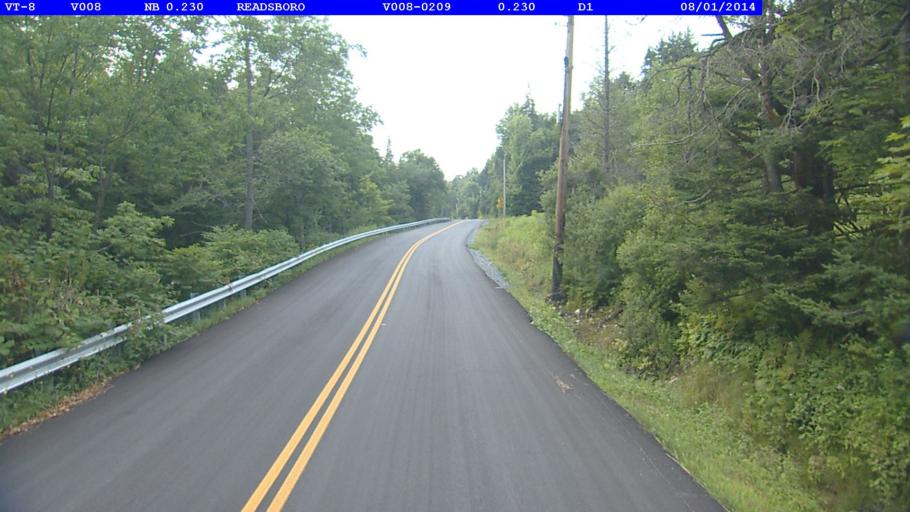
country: US
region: Massachusetts
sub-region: Berkshire County
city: North Adams
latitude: 42.8318
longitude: -72.9882
